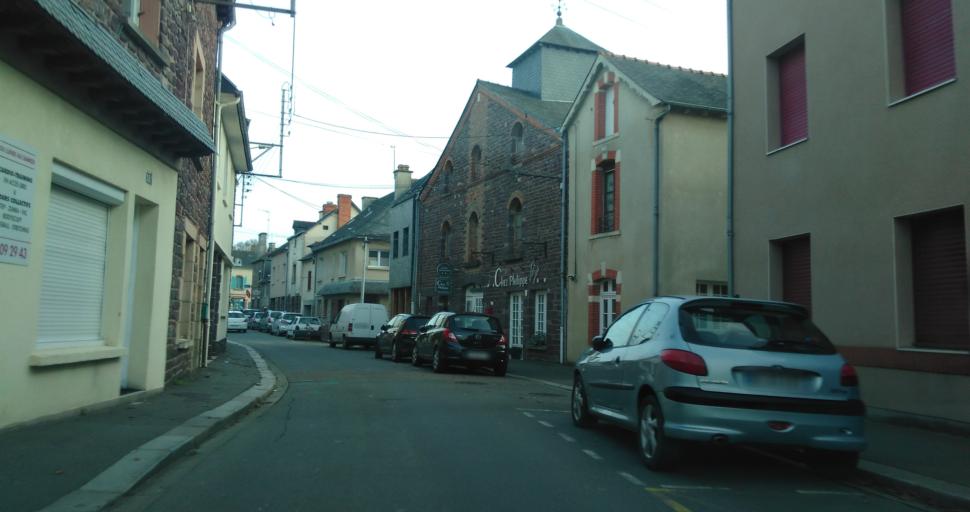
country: FR
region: Brittany
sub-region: Departement d'Ille-et-Vilaine
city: Montfort-sur-Meu
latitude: 48.1382
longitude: -1.9588
